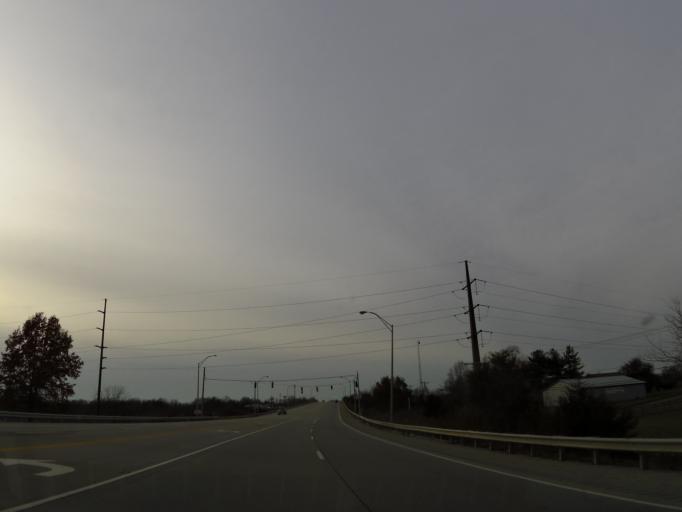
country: US
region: Kentucky
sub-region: Scott County
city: Georgetown
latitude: 38.2716
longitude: -84.5438
